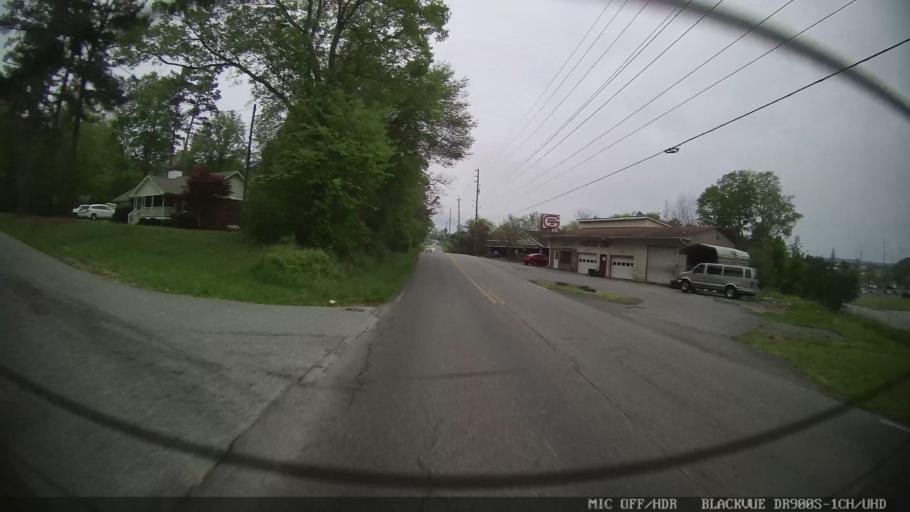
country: US
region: Georgia
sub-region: Bartow County
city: Cartersville
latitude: 34.2038
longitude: -84.7818
